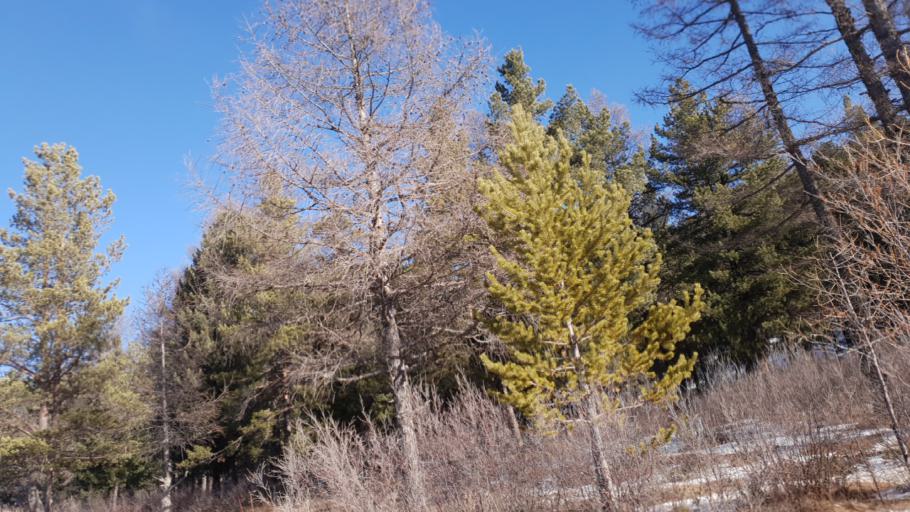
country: MN
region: Ulaanbaatar
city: Ulaanbaatar
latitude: 48.1593
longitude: 106.8823
